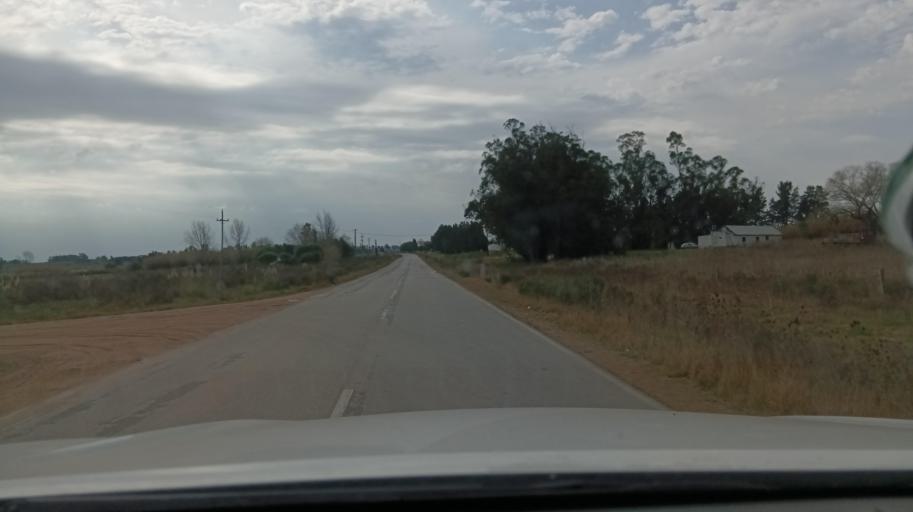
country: UY
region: Canelones
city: Sauce
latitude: -34.6480
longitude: -56.1066
